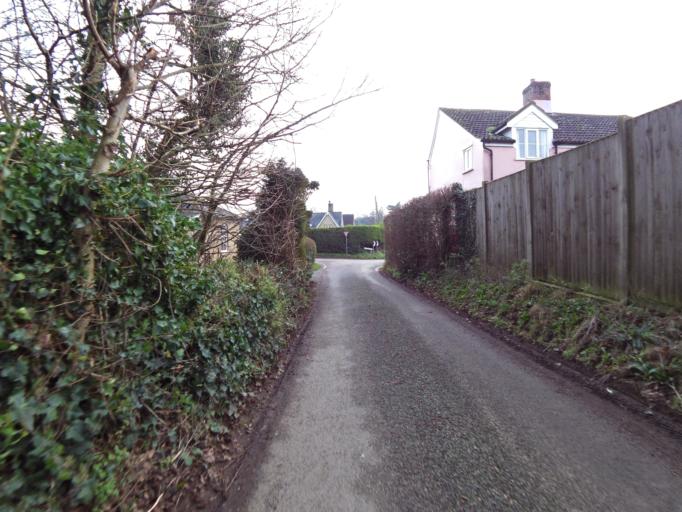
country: GB
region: England
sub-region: Suffolk
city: Woodbridge
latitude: 52.0563
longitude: 1.3190
